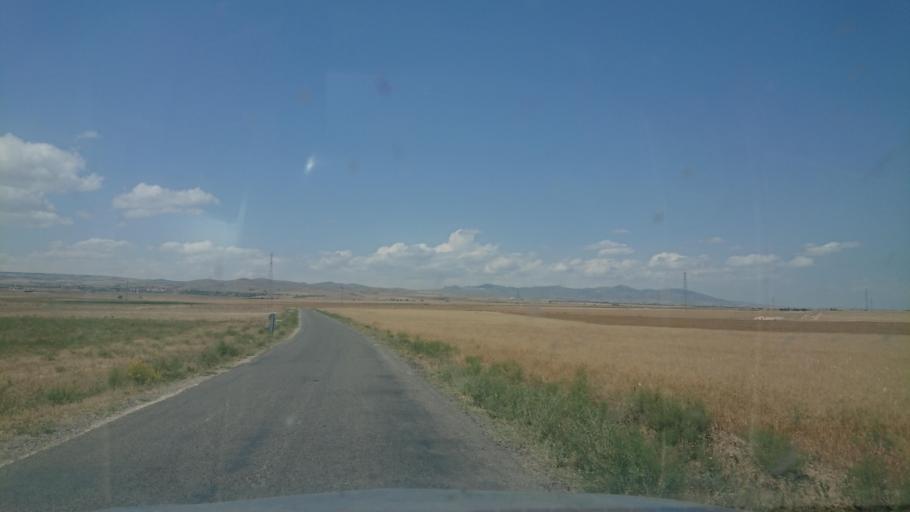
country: TR
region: Aksaray
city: Sariyahsi
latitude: 39.0024
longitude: 33.8934
